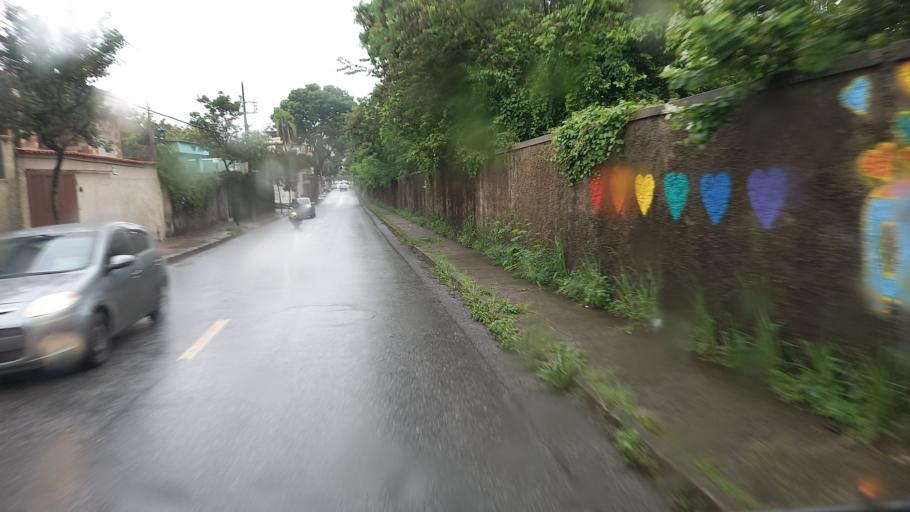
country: BR
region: Minas Gerais
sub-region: Belo Horizonte
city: Belo Horizonte
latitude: -19.8914
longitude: -43.9116
